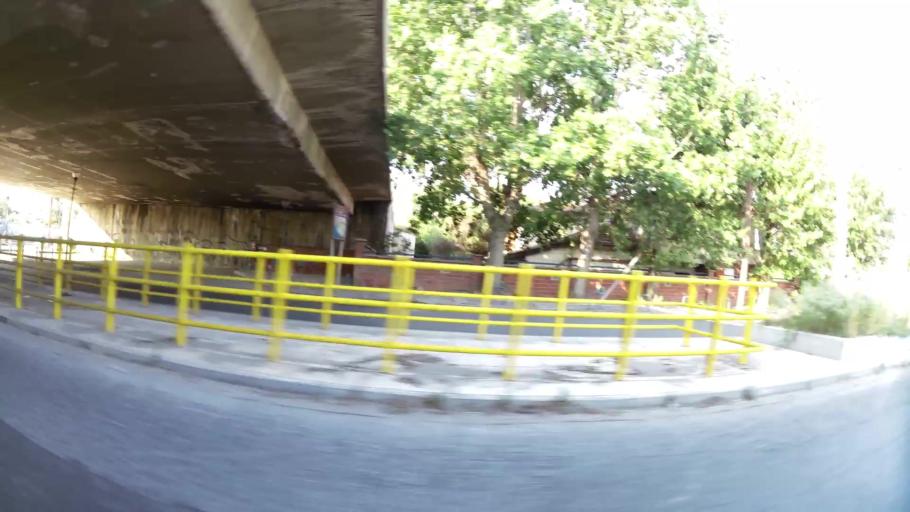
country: GR
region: Central Macedonia
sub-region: Nomos Thessalonikis
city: Menemeni
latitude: 40.6702
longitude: 22.8860
